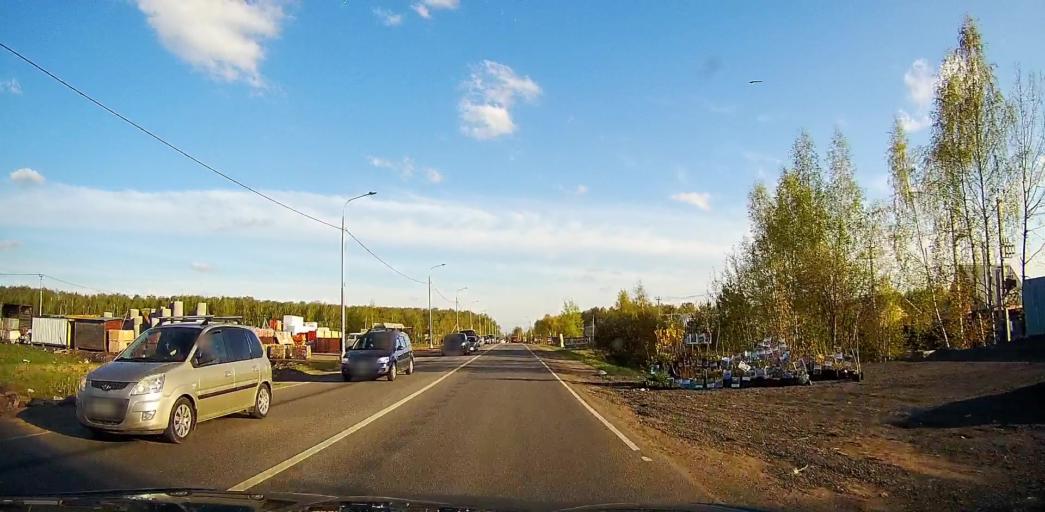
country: RU
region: Moskovskaya
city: Bronnitsy
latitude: 55.3851
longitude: 38.2066
